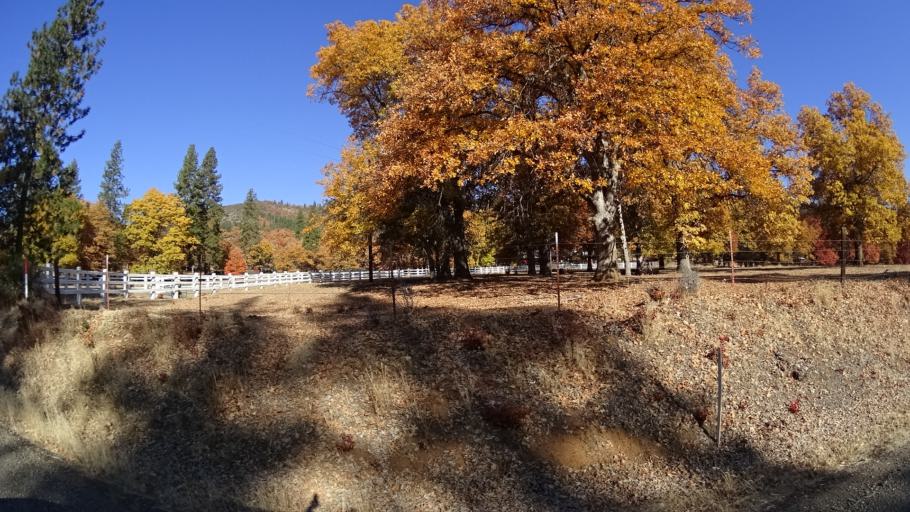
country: US
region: California
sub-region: Siskiyou County
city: Yreka
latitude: 41.6422
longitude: -122.9294
